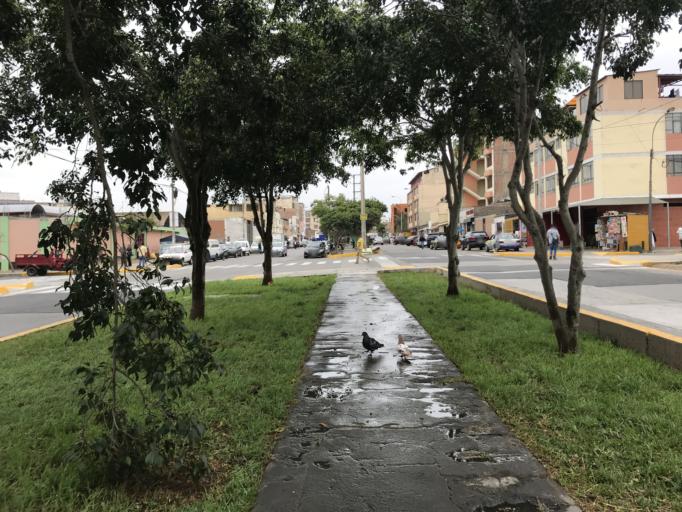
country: PE
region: Callao
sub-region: Callao
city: Callao
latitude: -12.0646
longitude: -77.0715
